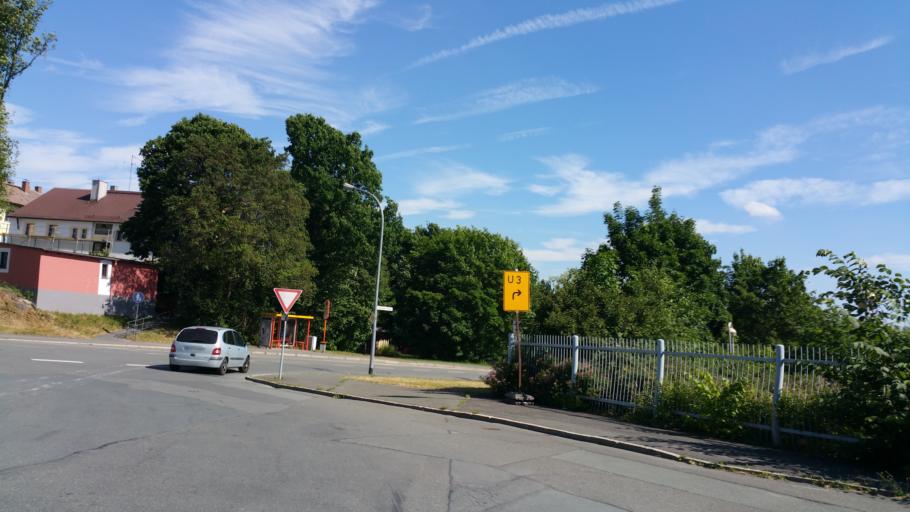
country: DE
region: Bavaria
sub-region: Upper Franconia
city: Dohlau
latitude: 50.2892
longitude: 11.9247
